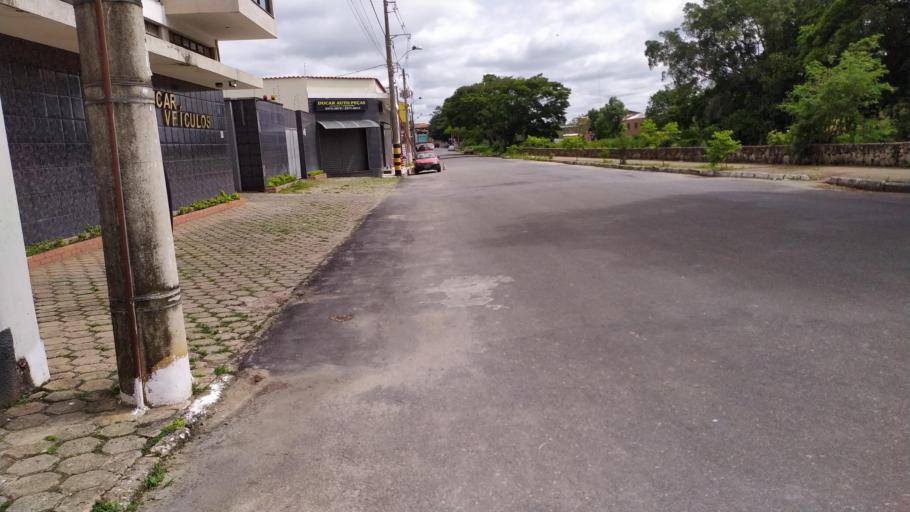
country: BR
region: Minas Gerais
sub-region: Sao Joao Del Rei
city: Sao Joao del Rei
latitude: -21.1243
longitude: -44.2456
